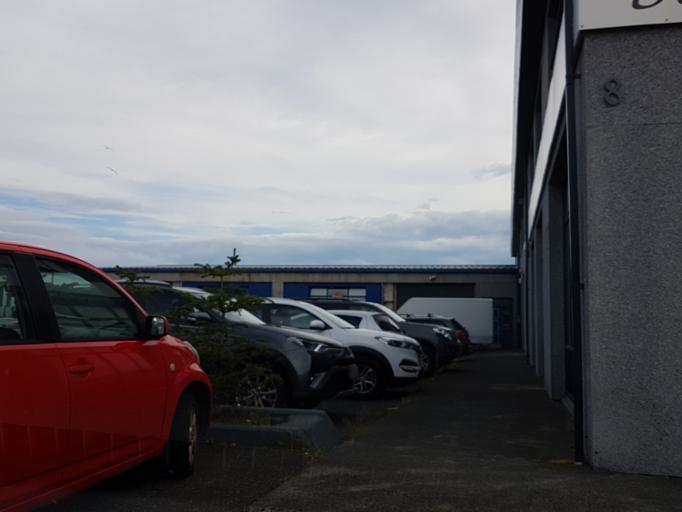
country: IS
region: Southern Peninsula
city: Reykjanesbaer
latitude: 64.0090
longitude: -22.5625
